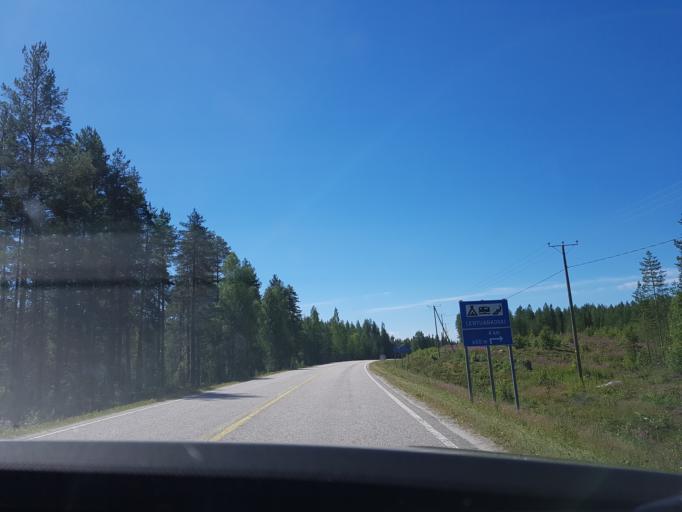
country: FI
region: Kainuu
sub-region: Kehys-Kainuu
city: Kuhmo
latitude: 64.1722
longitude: 29.6588
